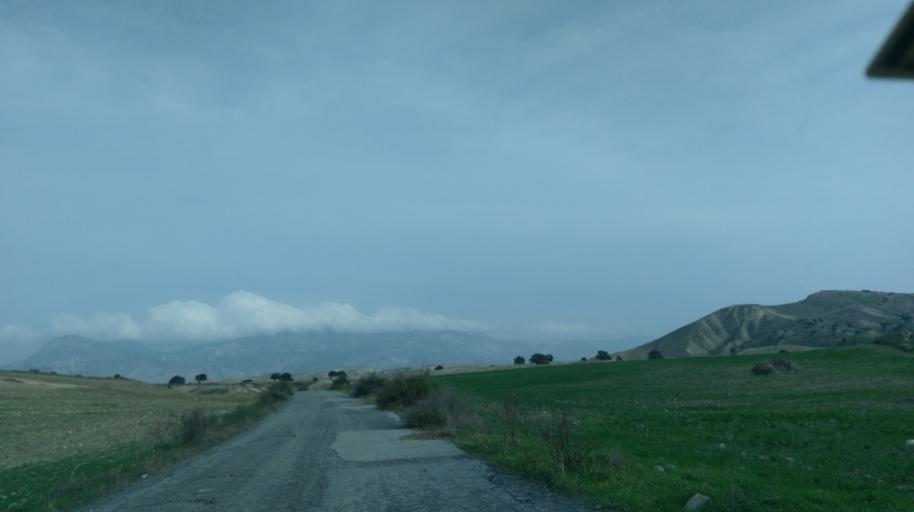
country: CY
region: Lefkosia
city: Morfou
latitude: 35.2572
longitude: 33.0870
